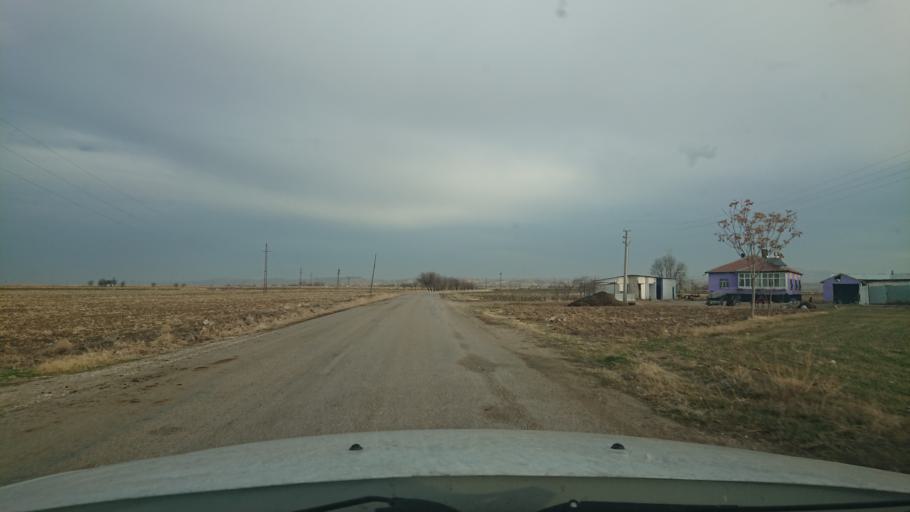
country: TR
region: Aksaray
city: Yesilova
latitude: 38.4284
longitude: 33.8352
